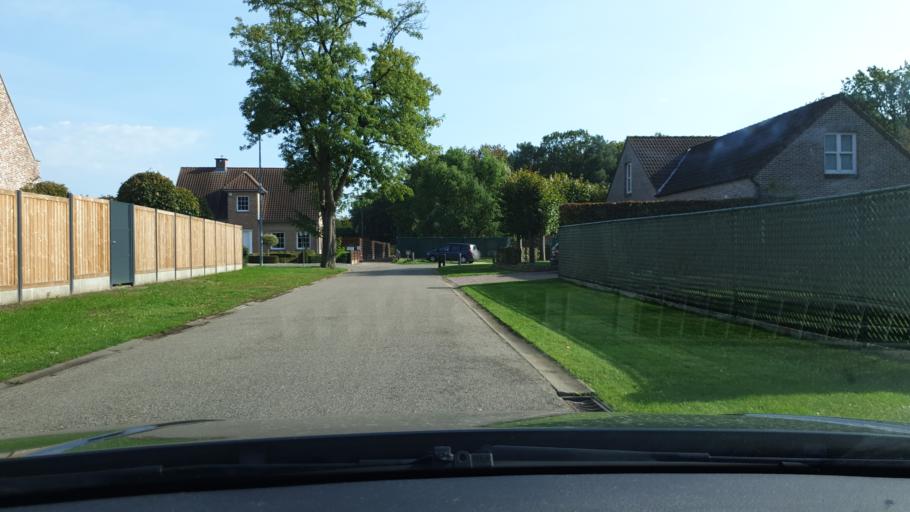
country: BE
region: Flanders
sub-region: Provincie Antwerpen
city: Geel
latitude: 51.1291
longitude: 5.0012
